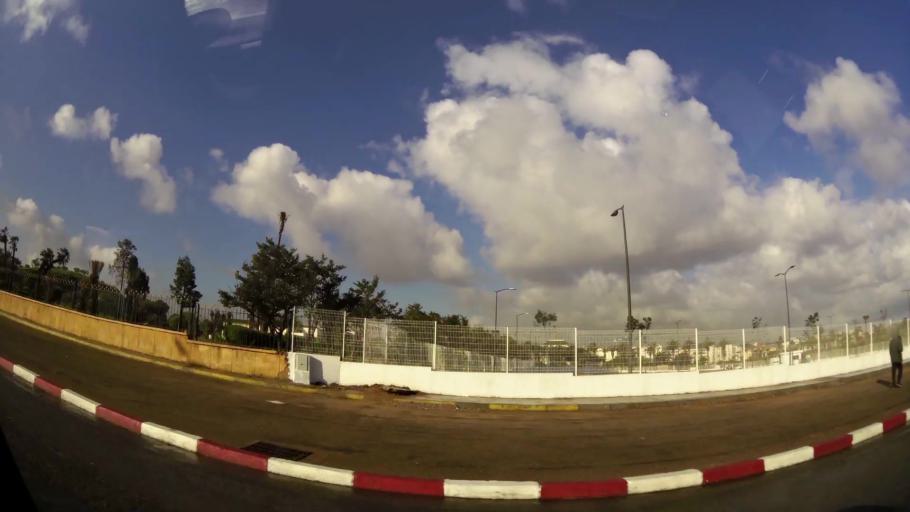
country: MA
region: Grand Casablanca
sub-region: Mediouna
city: Tit Mellil
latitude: 33.6013
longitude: -7.5270
